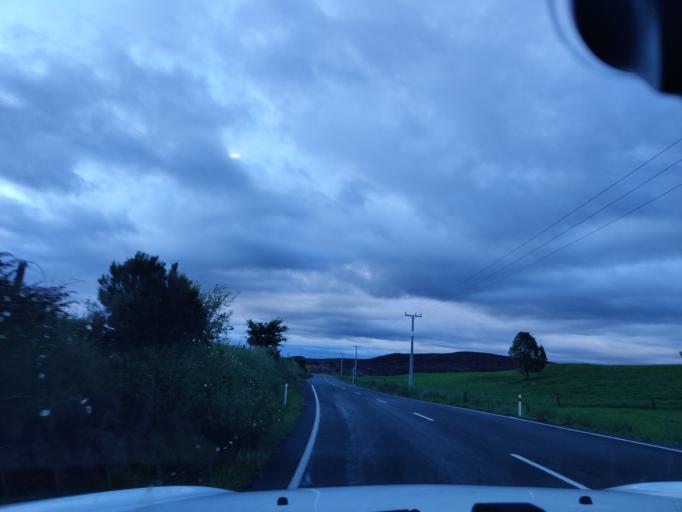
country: NZ
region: Waikato
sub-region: South Waikato District
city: Tokoroa
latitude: -38.1642
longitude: 175.7668
